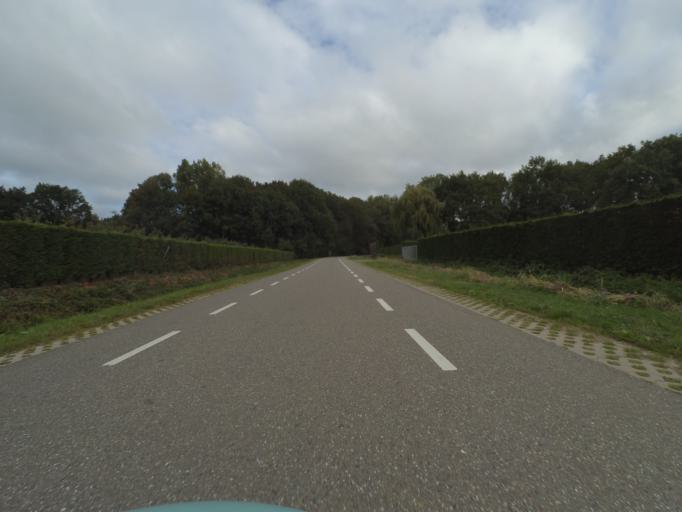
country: NL
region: Utrecht
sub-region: Gemeente Utrechtse Heuvelrug
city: Amerongen
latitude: 51.9625
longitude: 5.4609
